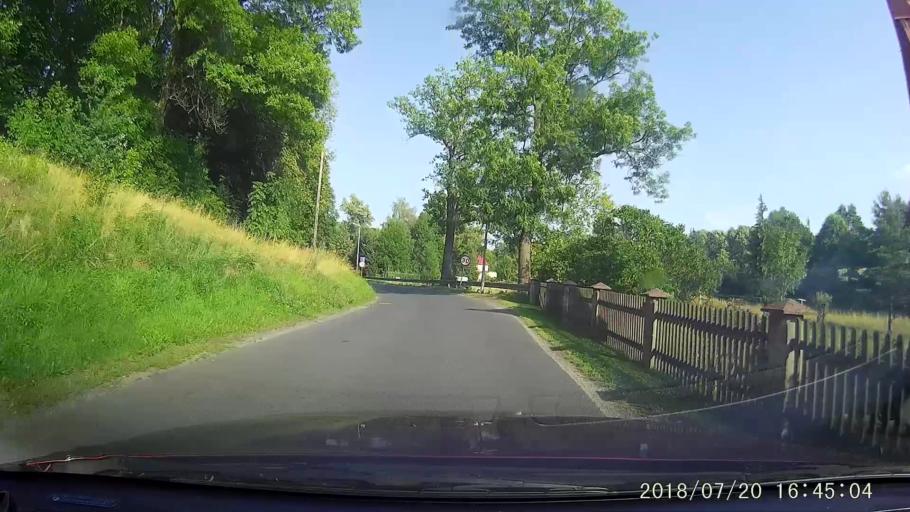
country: PL
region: Lower Silesian Voivodeship
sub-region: Powiat lubanski
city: Siekierczyn
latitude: 51.0666
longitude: 15.1702
